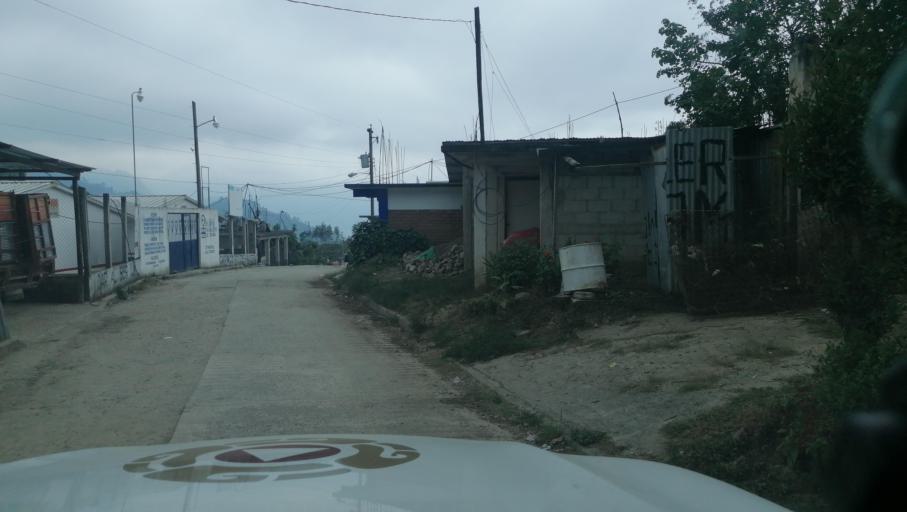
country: GT
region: San Marcos
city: Tacana
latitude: 15.2006
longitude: -92.1770
